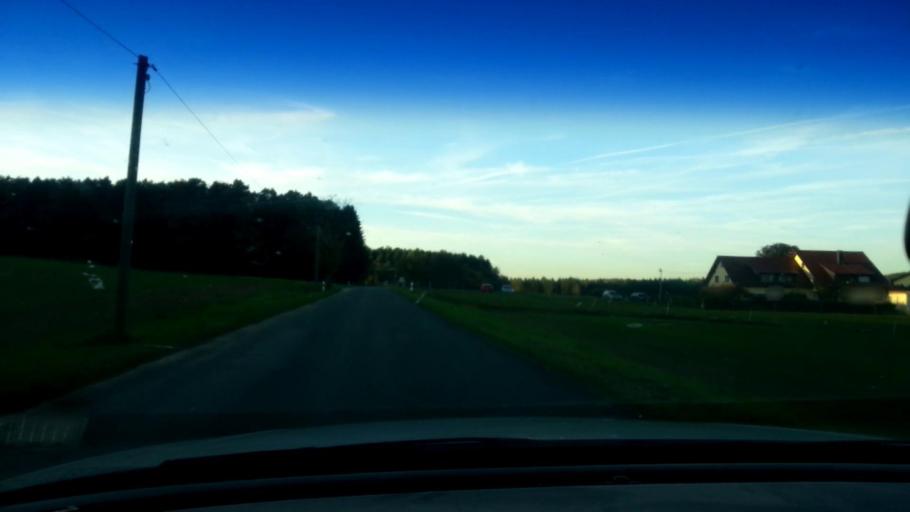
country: DE
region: Bavaria
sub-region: Upper Franconia
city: Unterleinleiter
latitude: 49.8332
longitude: 11.2118
